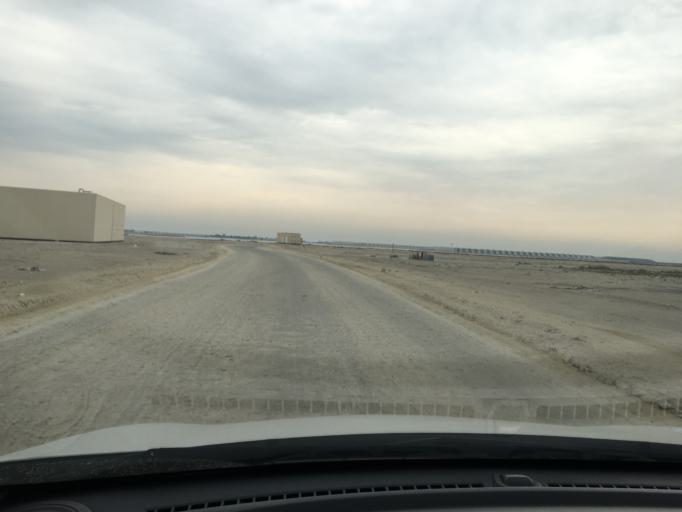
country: BH
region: Central Governorate
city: Dar Kulayb
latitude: 25.8373
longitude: 50.5909
